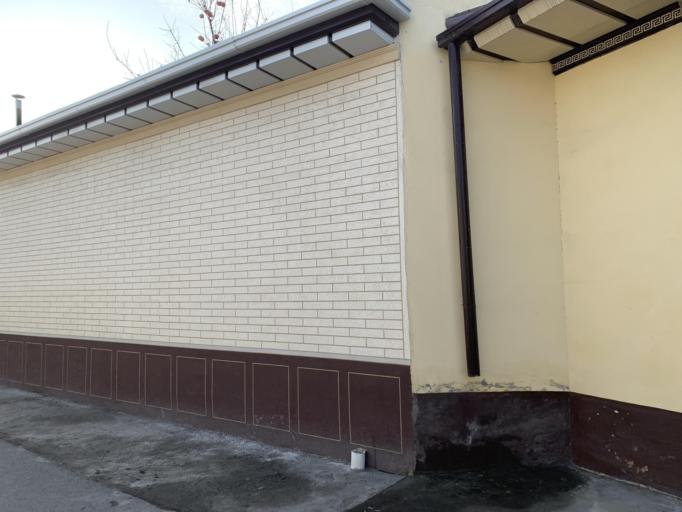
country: UZ
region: Fergana
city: Qo`qon
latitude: 40.5391
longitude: 70.9306
